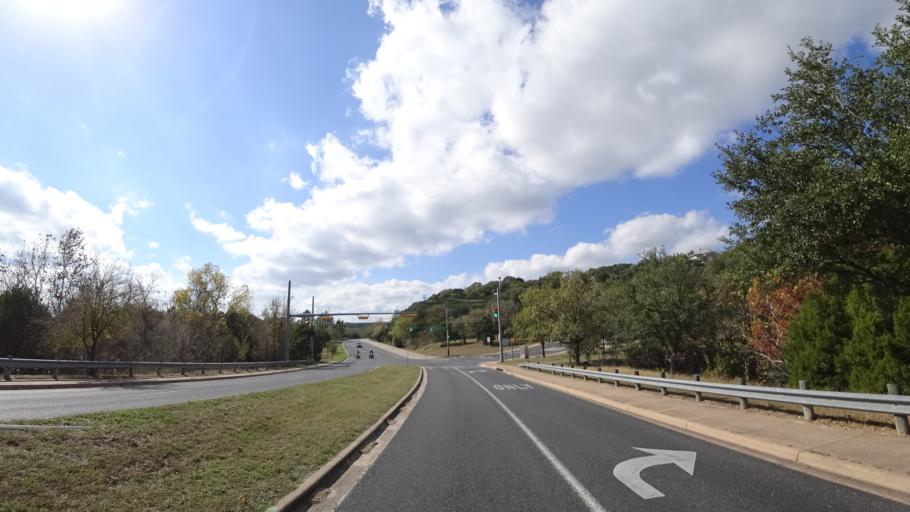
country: US
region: Texas
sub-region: Williamson County
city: Jollyville
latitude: 30.4227
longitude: -97.7931
